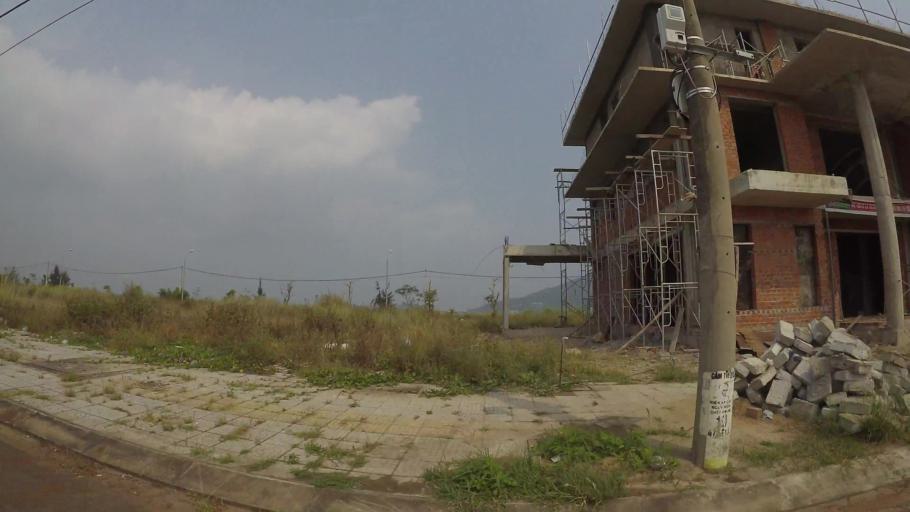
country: VN
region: Da Nang
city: Da Nang
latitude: 16.1029
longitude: 108.2338
